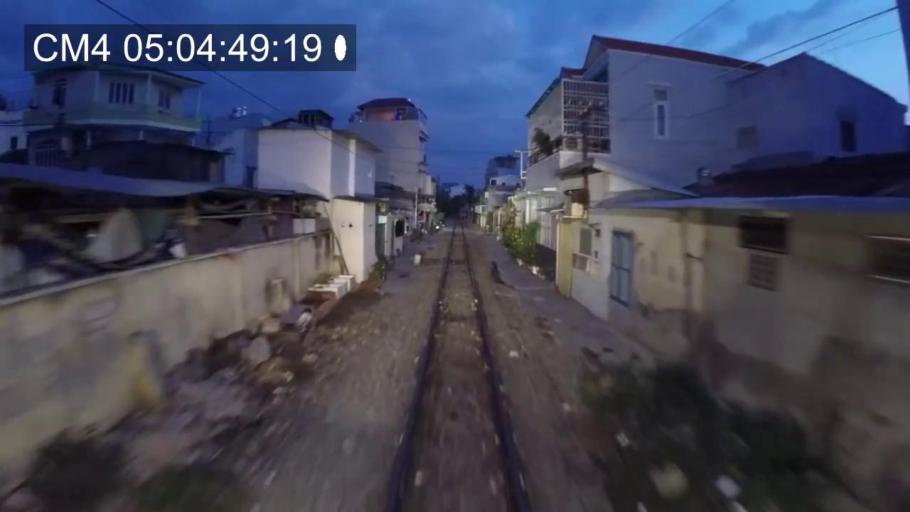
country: VN
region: Khanh Hoa
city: Nha Trang
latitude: 12.2668
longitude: 109.1733
